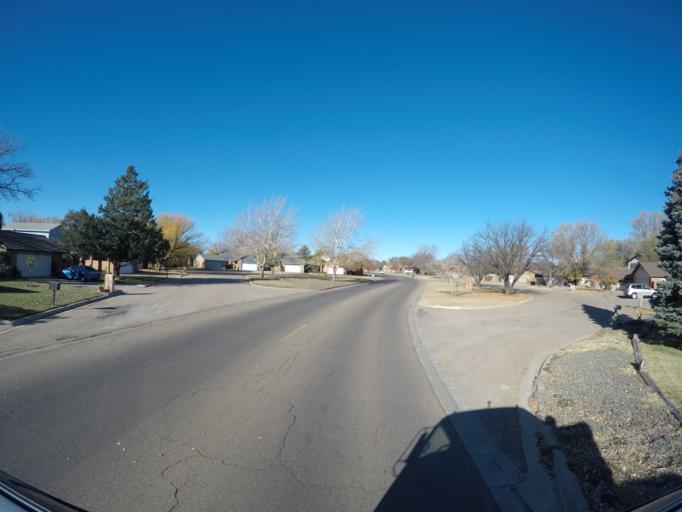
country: US
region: New Mexico
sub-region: Curry County
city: Clovis
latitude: 34.4405
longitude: -103.1817
